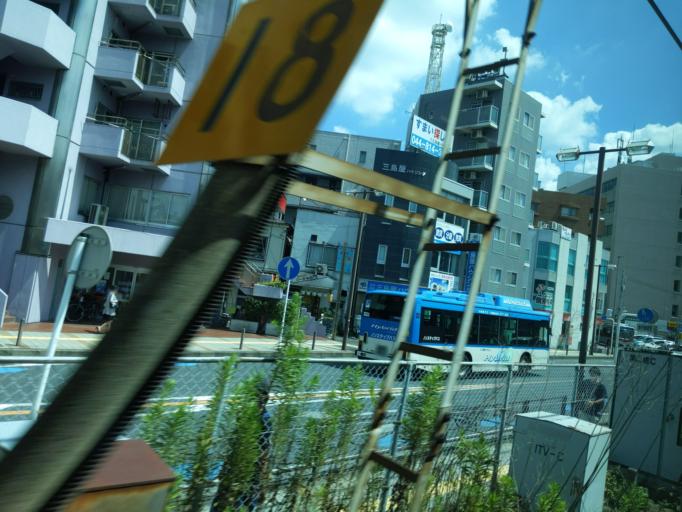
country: JP
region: Tokyo
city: Chofugaoka
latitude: 35.5977
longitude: 139.6130
